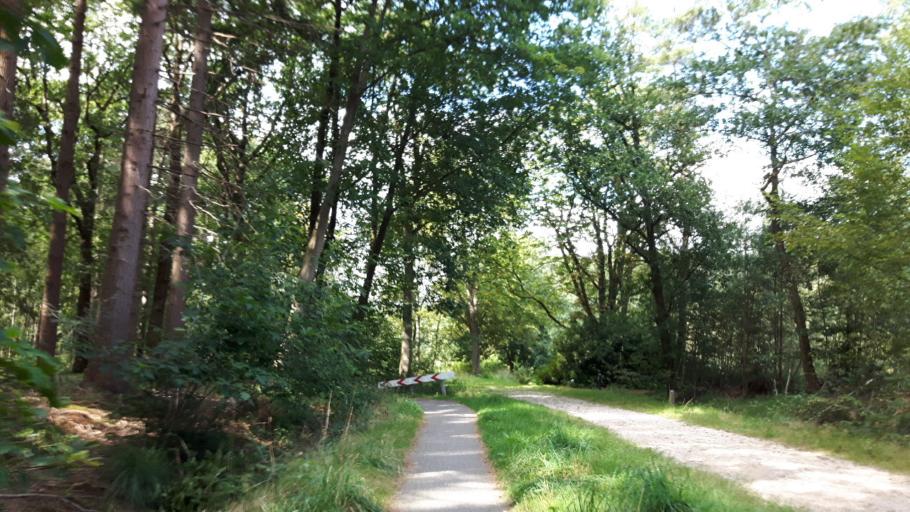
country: NL
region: Friesland
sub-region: Gemeente Smallingerland
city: Drachtstercompagnie
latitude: 53.0822
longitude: 6.2348
